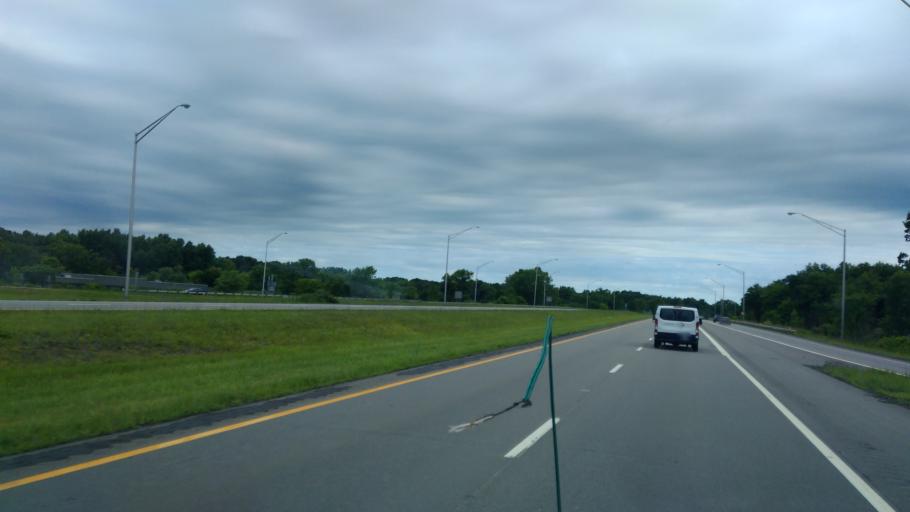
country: US
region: Ohio
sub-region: Mahoning County
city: Austintown
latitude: 41.1012
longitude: -80.7529
